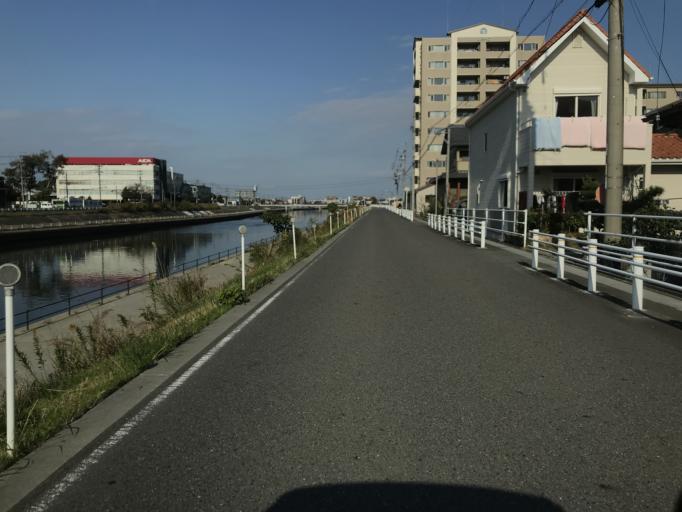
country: JP
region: Aichi
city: Nagoya-shi
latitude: 35.1874
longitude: 136.8475
